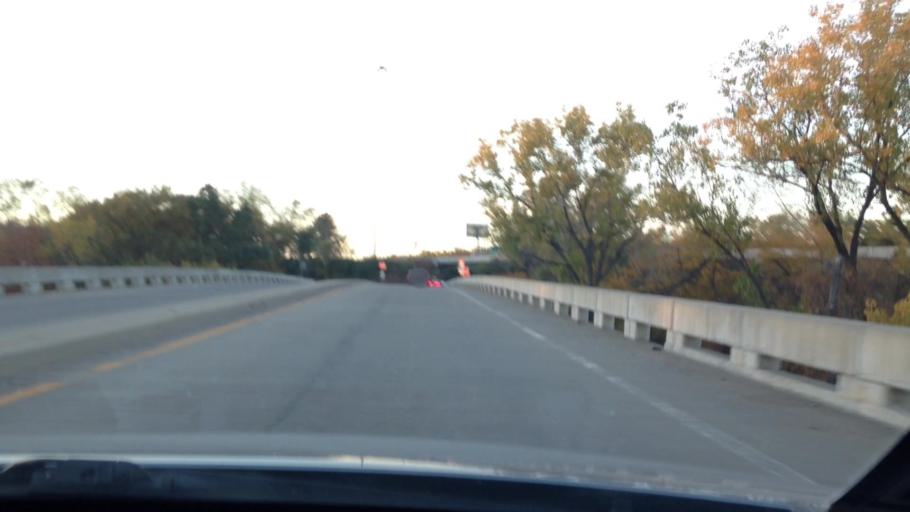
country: US
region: Kansas
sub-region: Wyandotte County
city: Kansas City
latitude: 39.1000
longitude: -94.6713
